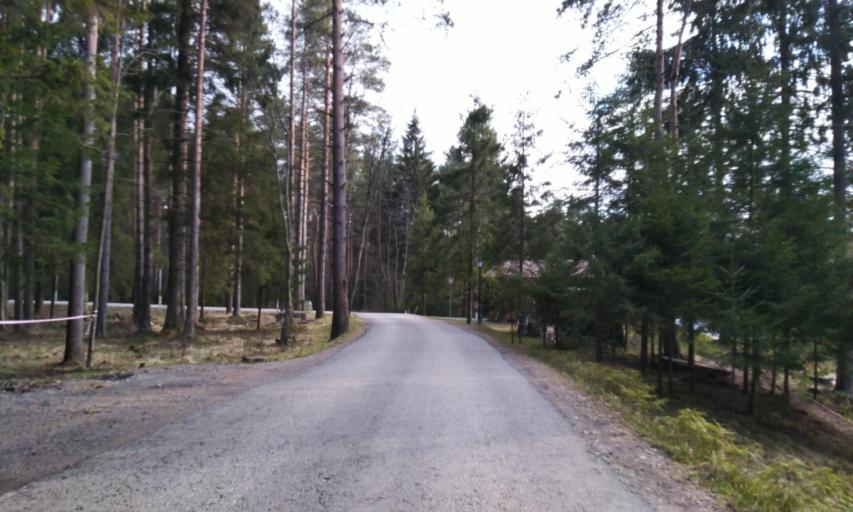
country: RU
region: Leningrad
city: Toksovo
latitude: 60.1286
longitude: 30.4530
